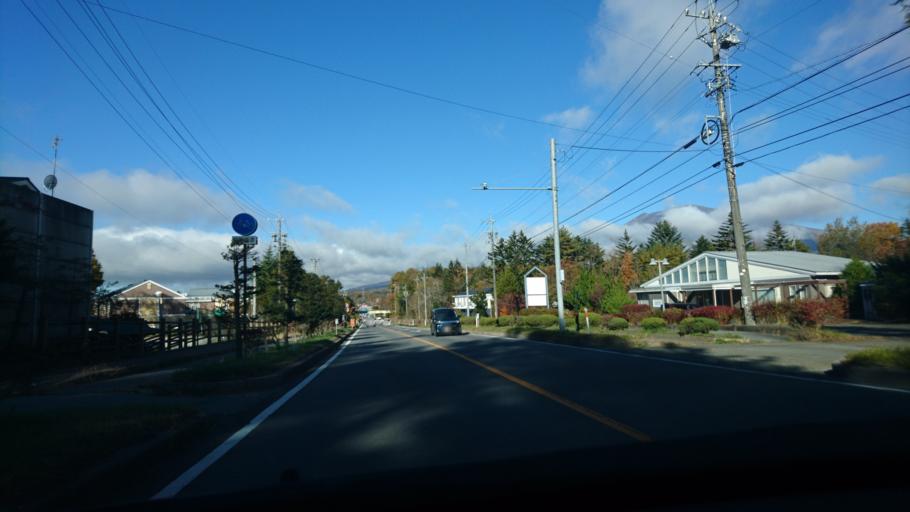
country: JP
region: Nagano
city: Saku
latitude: 36.3355
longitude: 138.5990
